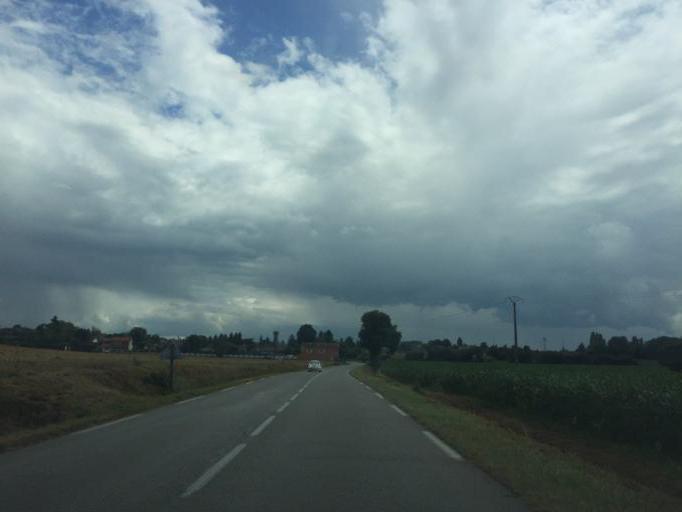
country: FR
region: Rhone-Alpes
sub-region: Departement du Rhone
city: Jons
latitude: 45.7964
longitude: 5.1045
